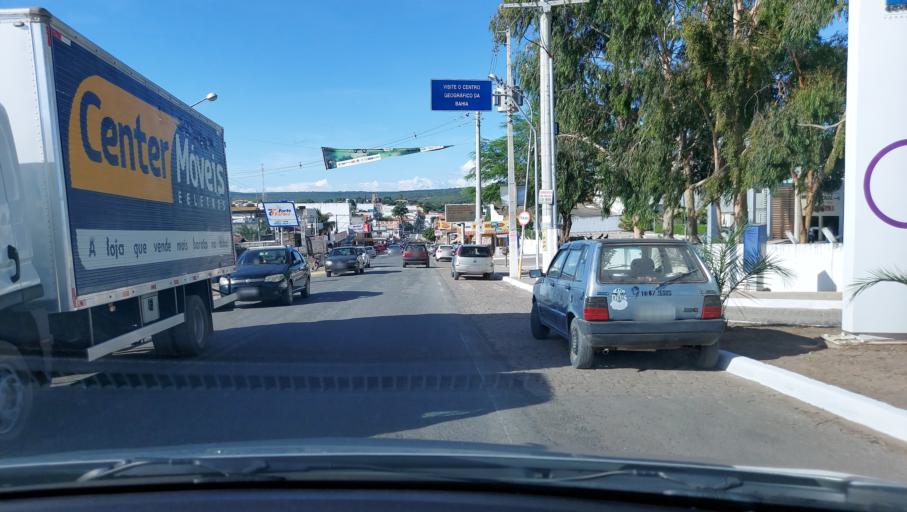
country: BR
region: Bahia
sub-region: Seabra
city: Seabra
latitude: -12.4255
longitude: -41.7693
